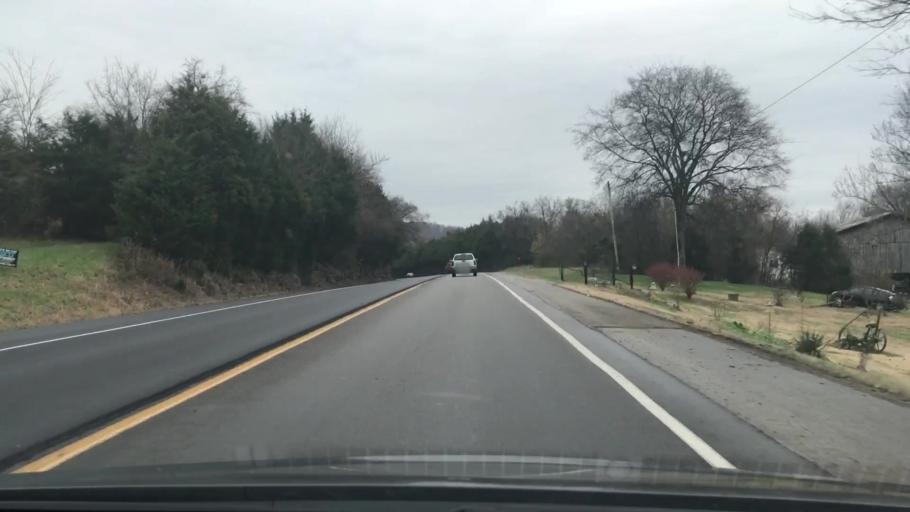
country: US
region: Tennessee
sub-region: Smith County
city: Carthage
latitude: 36.3284
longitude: -86.0225
